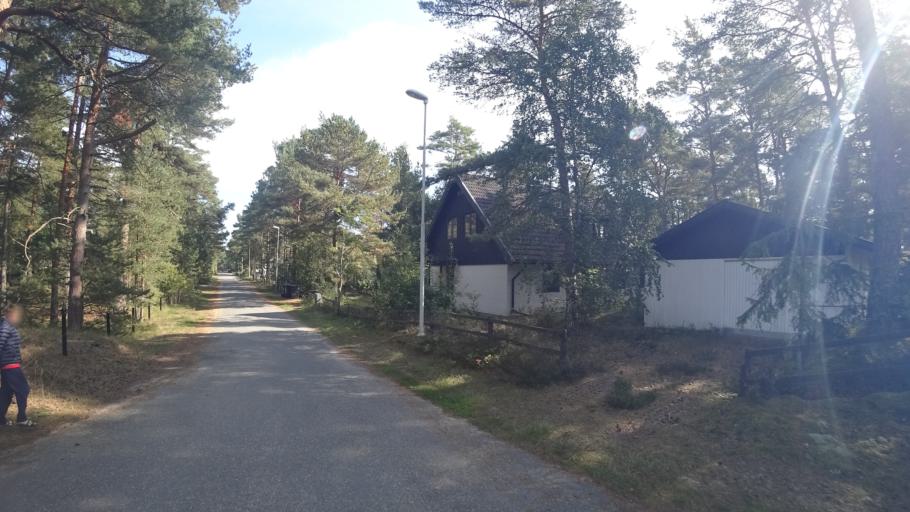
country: SE
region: Skane
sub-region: Kristianstads Kommun
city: Ahus
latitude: 55.9071
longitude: 14.2899
